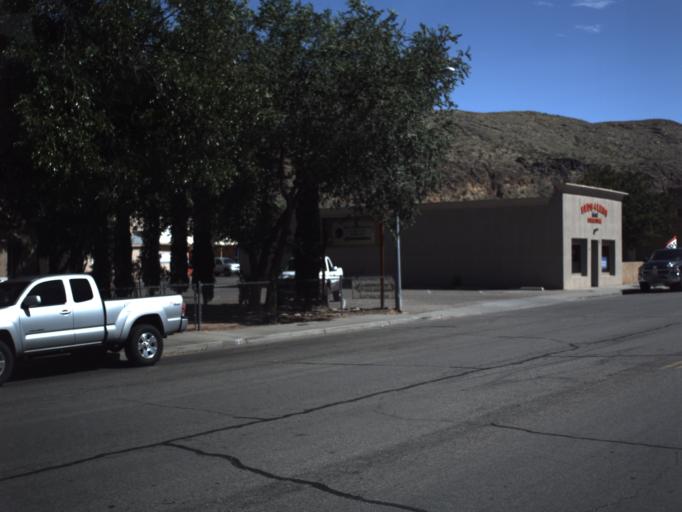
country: US
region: Utah
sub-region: Washington County
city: Hurricane
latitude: 37.1777
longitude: -113.2882
